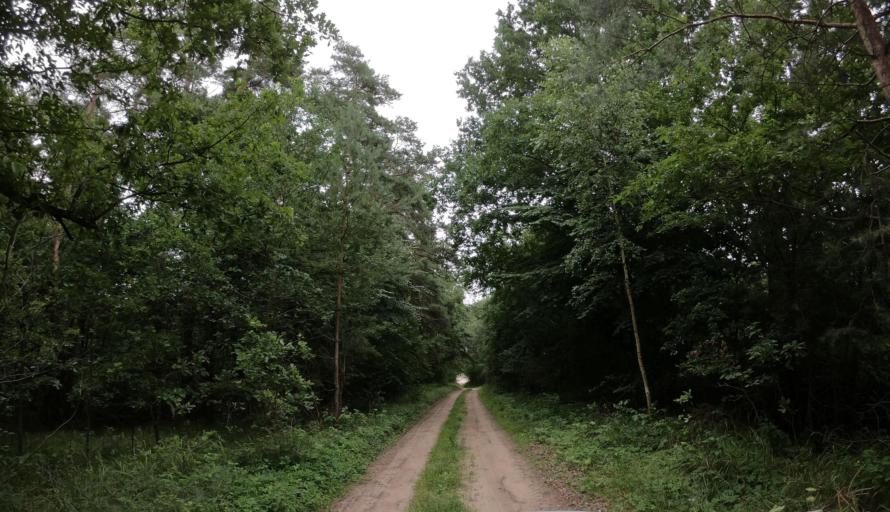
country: PL
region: West Pomeranian Voivodeship
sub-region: Powiat goleniowski
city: Przybiernow
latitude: 53.8251
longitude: 14.7470
